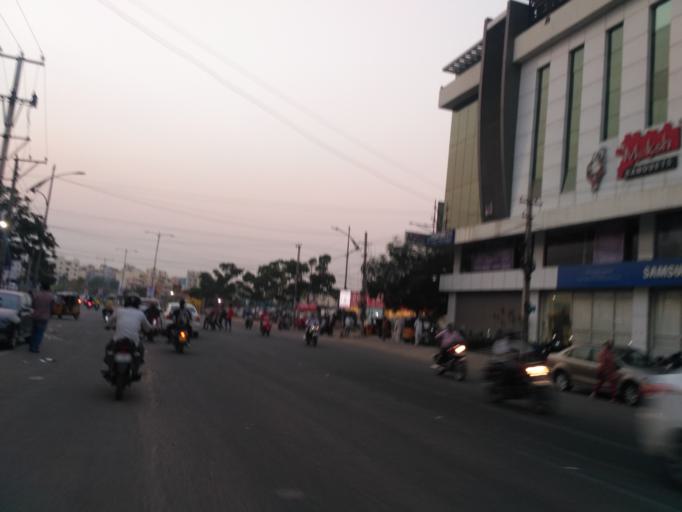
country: IN
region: Telangana
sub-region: Rangareddi
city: Kukatpalli
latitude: 17.4422
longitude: 78.3963
